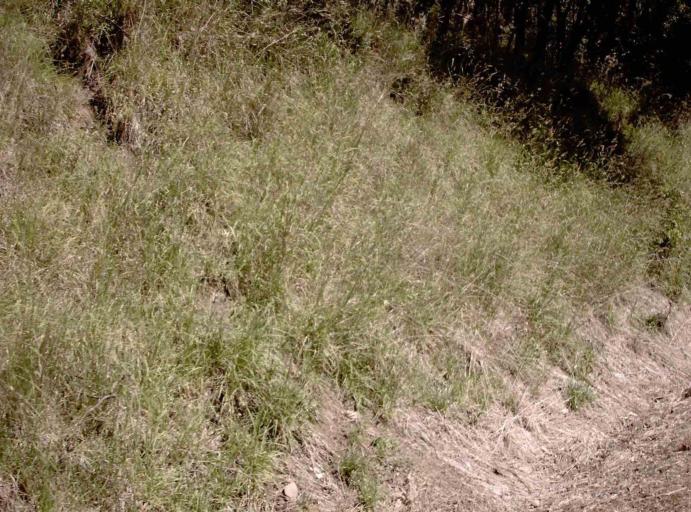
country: AU
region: Victoria
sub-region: East Gippsland
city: Lakes Entrance
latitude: -37.3442
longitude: 148.2299
